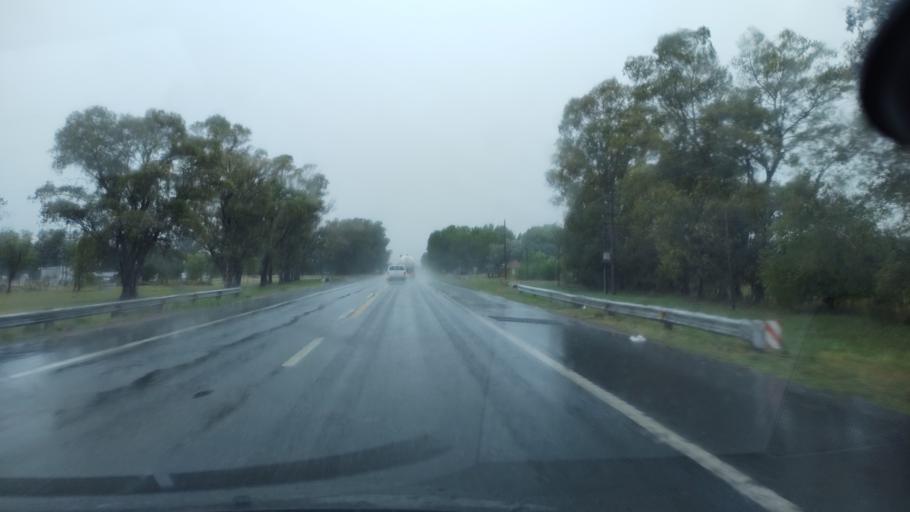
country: AR
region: Buenos Aires
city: Canuelas
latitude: -35.0329
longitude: -58.7526
